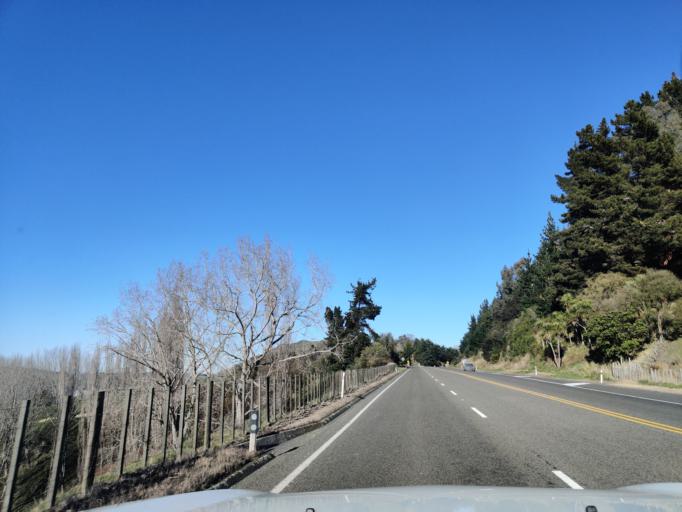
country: NZ
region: Manawatu-Wanganui
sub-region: Ruapehu District
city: Waiouru
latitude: -39.7662
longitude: 175.8011
